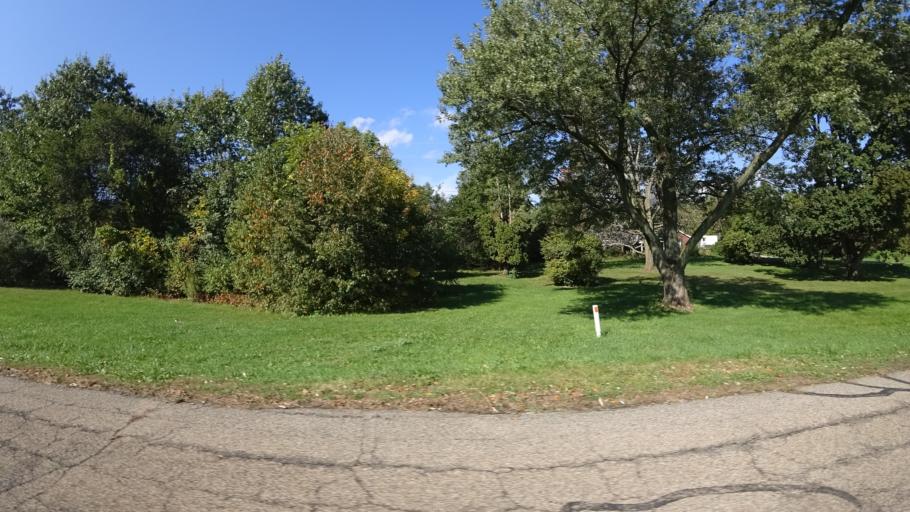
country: US
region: Michigan
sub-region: Jackson County
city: Spring Arbor
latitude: 42.2127
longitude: -84.5240
